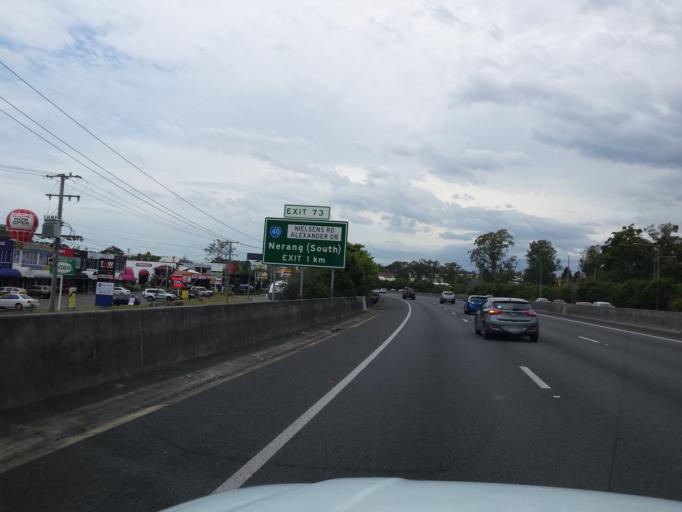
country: AU
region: Queensland
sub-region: Gold Coast
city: Nerang
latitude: -28.0018
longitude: 153.3398
